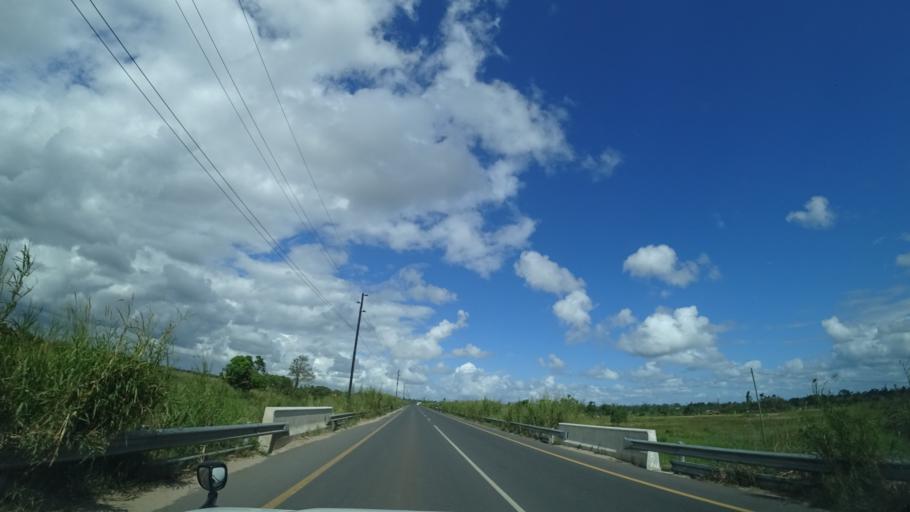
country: MZ
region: Sofala
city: Dondo
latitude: -19.5202
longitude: 34.6217
